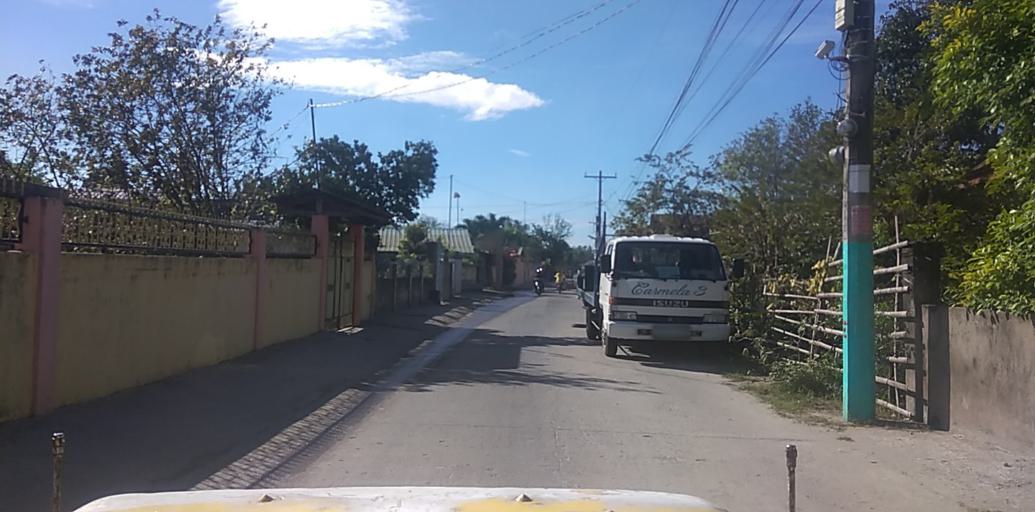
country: PH
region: Central Luzon
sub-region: Province of Pampanga
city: San Patricio
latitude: 15.1029
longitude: 120.7138
